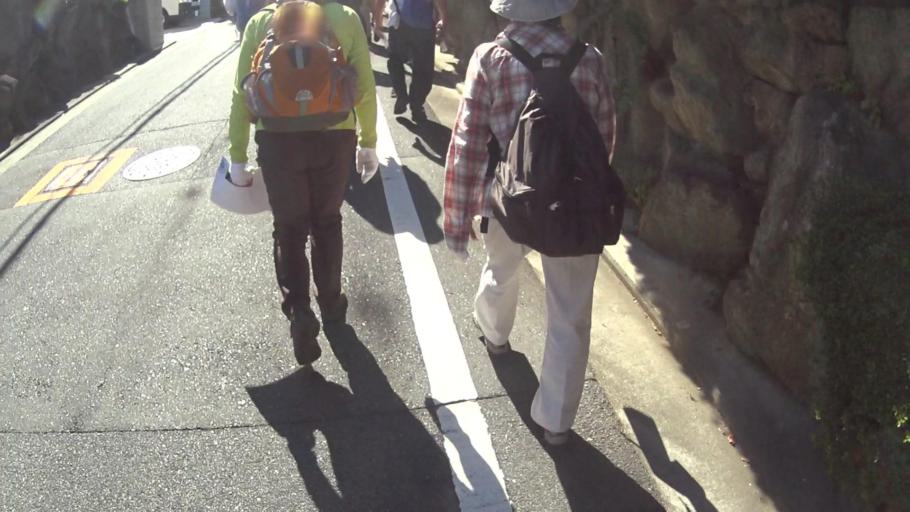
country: JP
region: Osaka
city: Izumi
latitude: 34.4975
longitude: 135.4271
